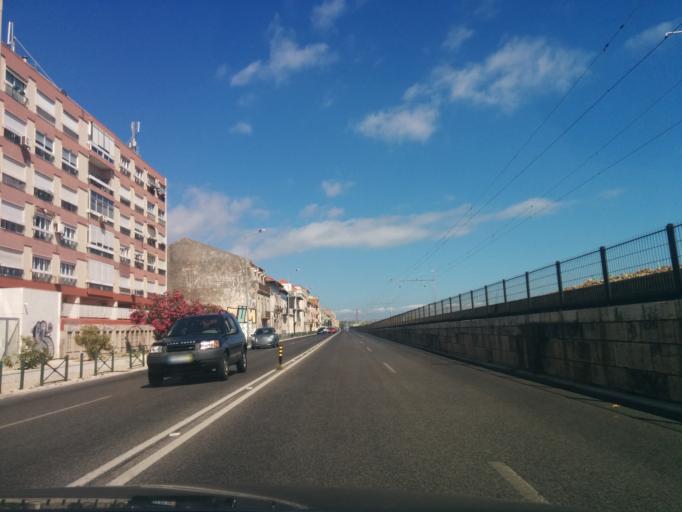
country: PT
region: Lisbon
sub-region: Oeiras
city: Linda-a-Velha
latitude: 38.6997
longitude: -9.2483
